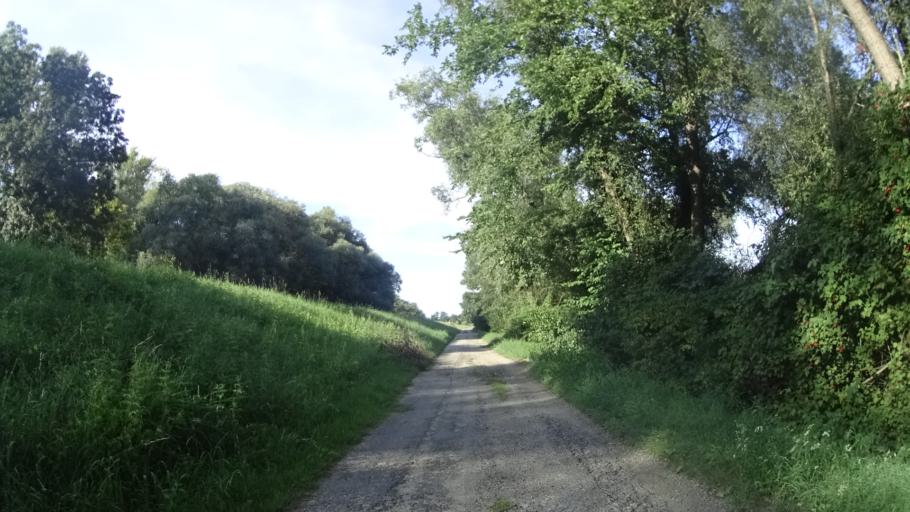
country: AT
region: Lower Austria
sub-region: Politischer Bezirk Ganserndorf
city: Drosing
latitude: 48.5447
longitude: 16.9613
